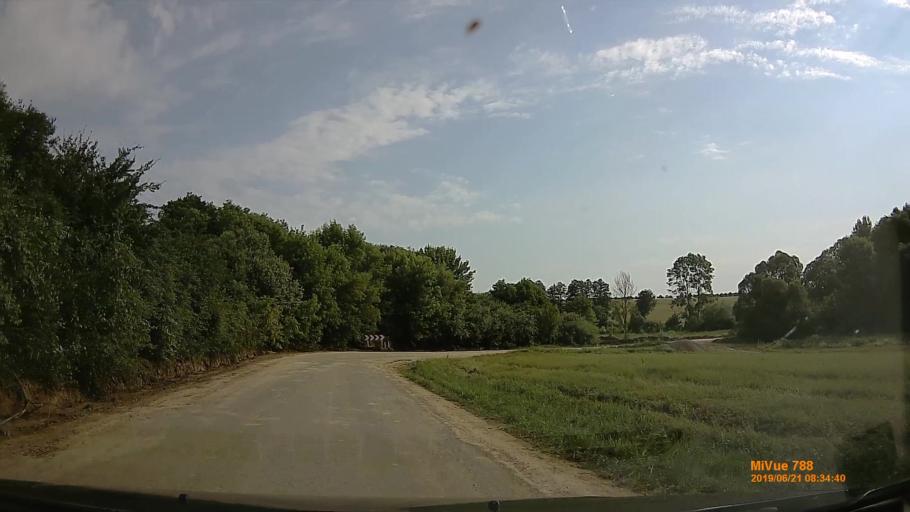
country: HU
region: Baranya
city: Buekkoesd
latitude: 46.1695
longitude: 17.8889
